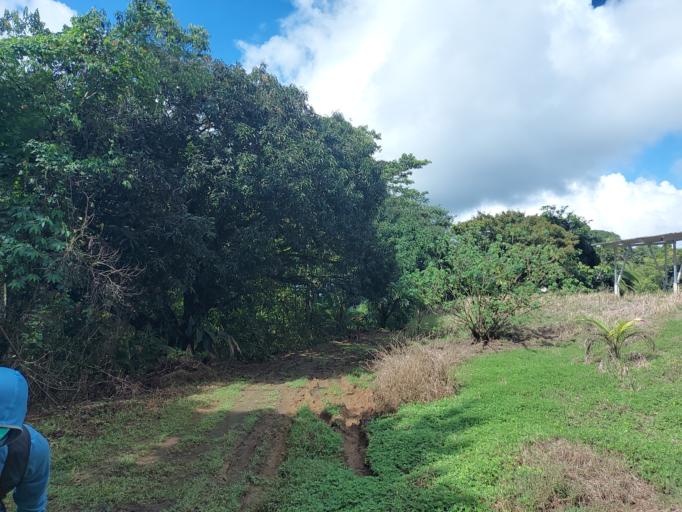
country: CR
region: Puntarenas
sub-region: Canton de Golfito
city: Golfito
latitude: 8.5773
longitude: -83.4851
